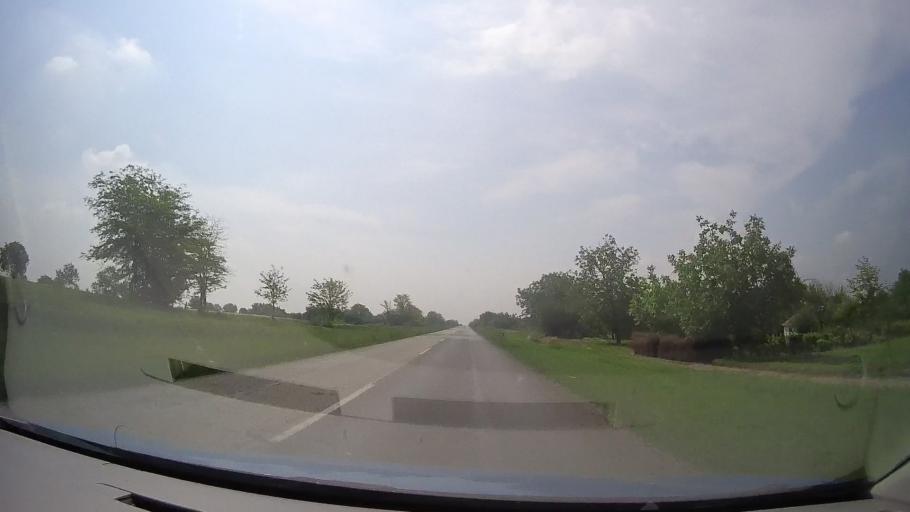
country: RS
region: Autonomna Pokrajina Vojvodina
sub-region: Juznobanatski Okrug
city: Kovacica
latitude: 45.0964
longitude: 20.6287
